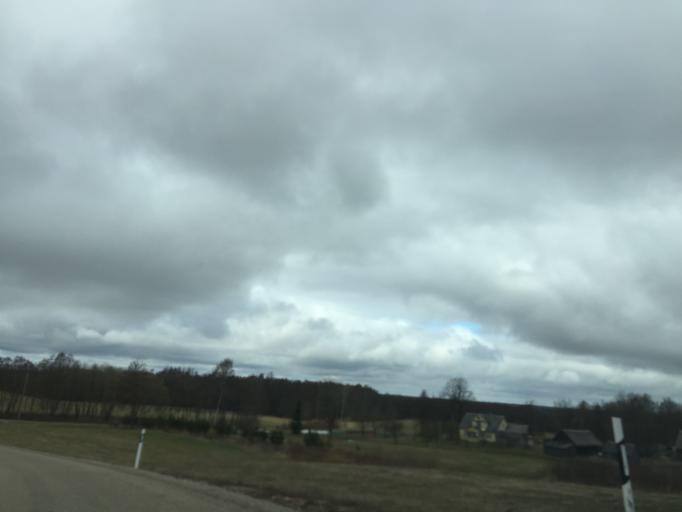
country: LV
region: Ilukste
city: Ilukste
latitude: 56.0573
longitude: 26.1755
